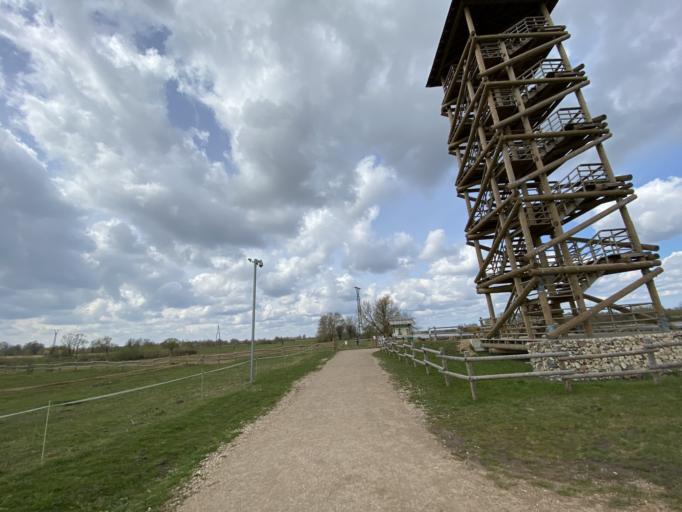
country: LV
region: Jelgava
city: Jelgava
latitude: 56.6627
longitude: 23.7261
